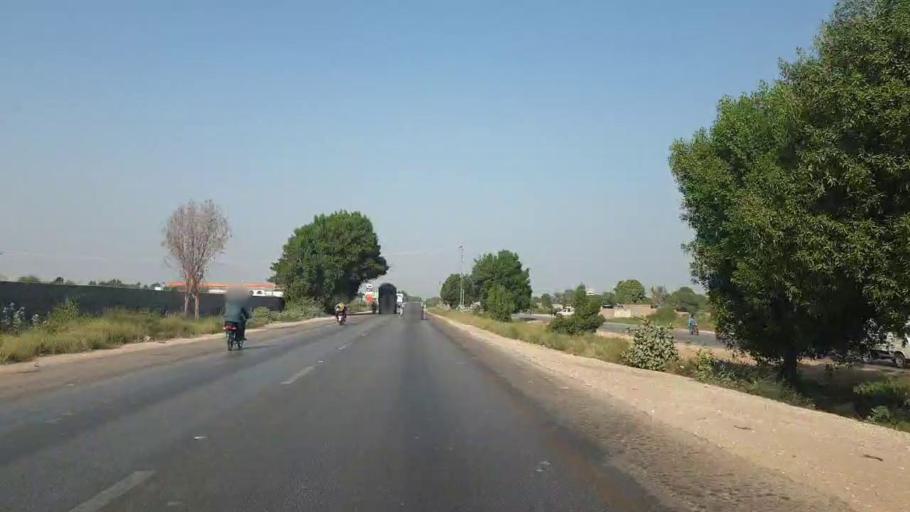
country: PK
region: Sindh
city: Matiari
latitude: 25.4963
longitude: 68.4237
